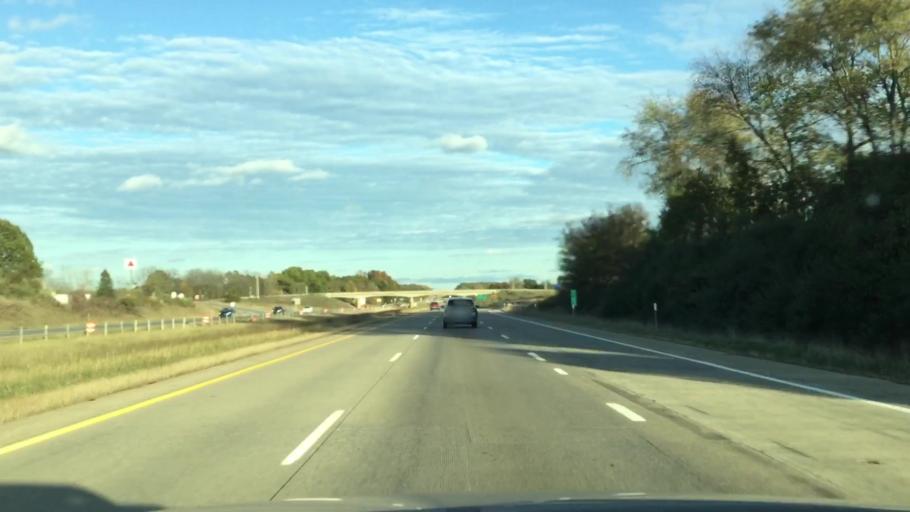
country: US
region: Michigan
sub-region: Calhoun County
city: Marshall
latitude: 42.2829
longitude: -84.8675
